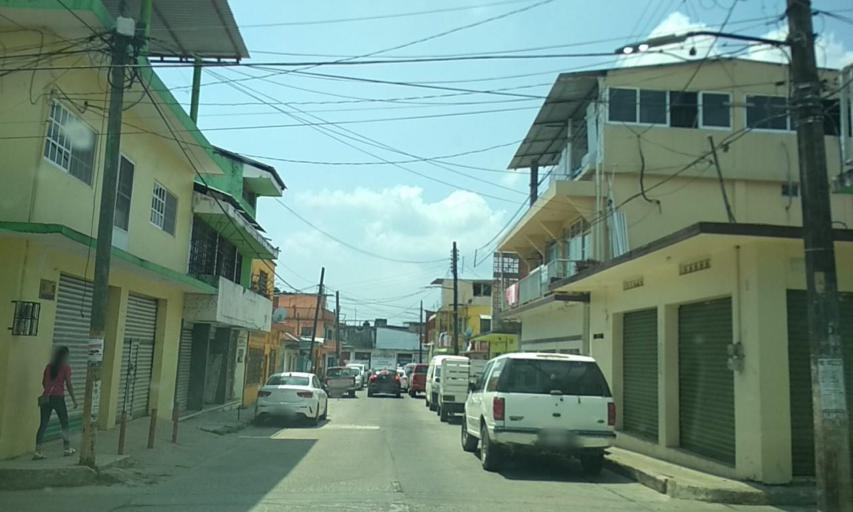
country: MX
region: Veracruz
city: Las Choapas
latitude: 17.9109
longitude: -94.0897
